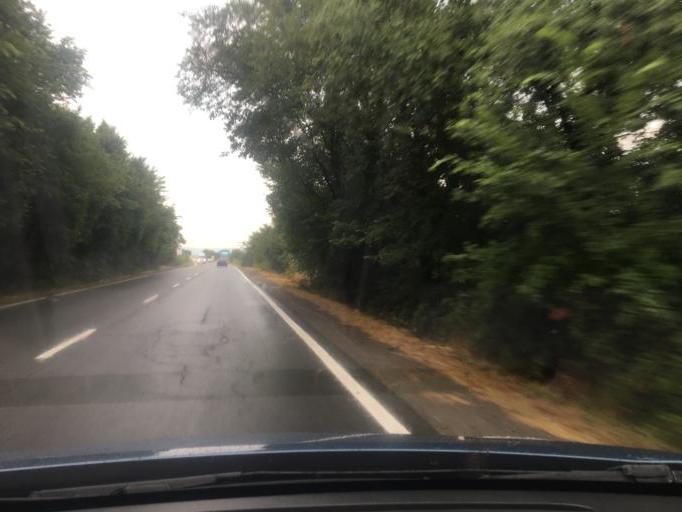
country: BG
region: Burgas
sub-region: Obshtina Pomorie
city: Pomorie
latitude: 42.5872
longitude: 27.6103
